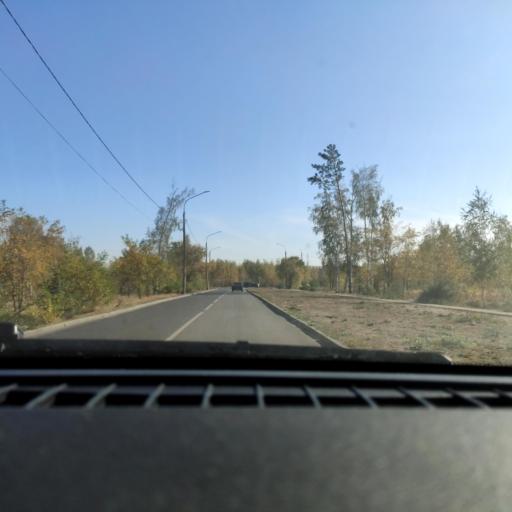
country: RU
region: Voronezj
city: Maslovka
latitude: 51.5871
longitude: 39.2459
